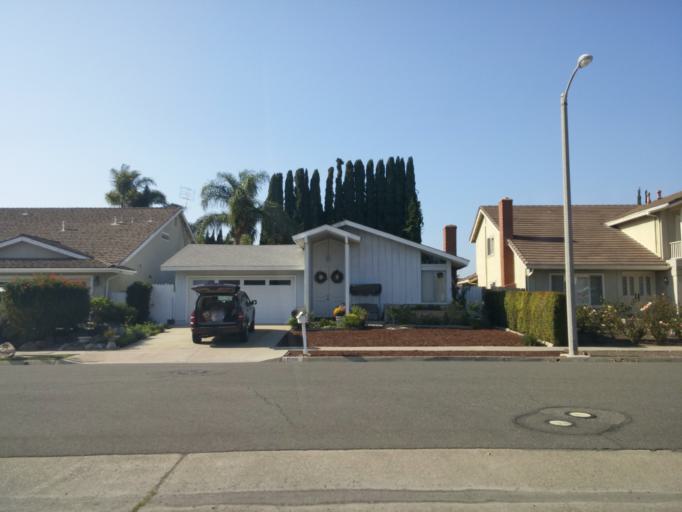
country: US
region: California
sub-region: Orange County
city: Irvine
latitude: 33.6864
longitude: -117.7769
